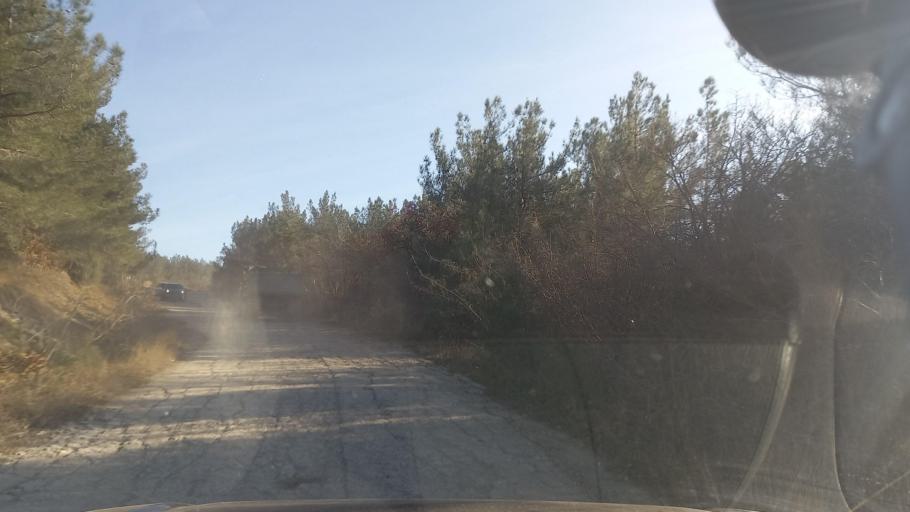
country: RU
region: Krasnodarskiy
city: Kabardinka
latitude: 44.6294
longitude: 37.9147
